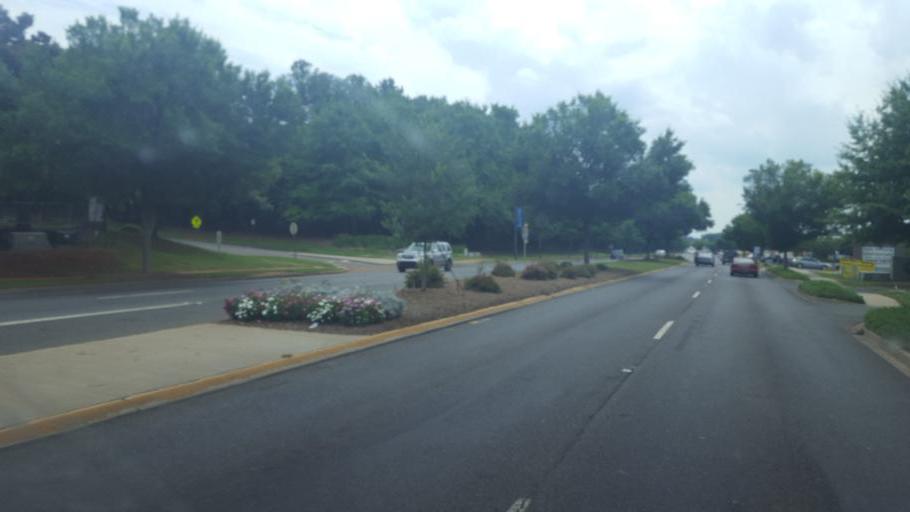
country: US
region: South Carolina
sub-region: York County
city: Rock Hill
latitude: 34.9592
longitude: -81.0074
